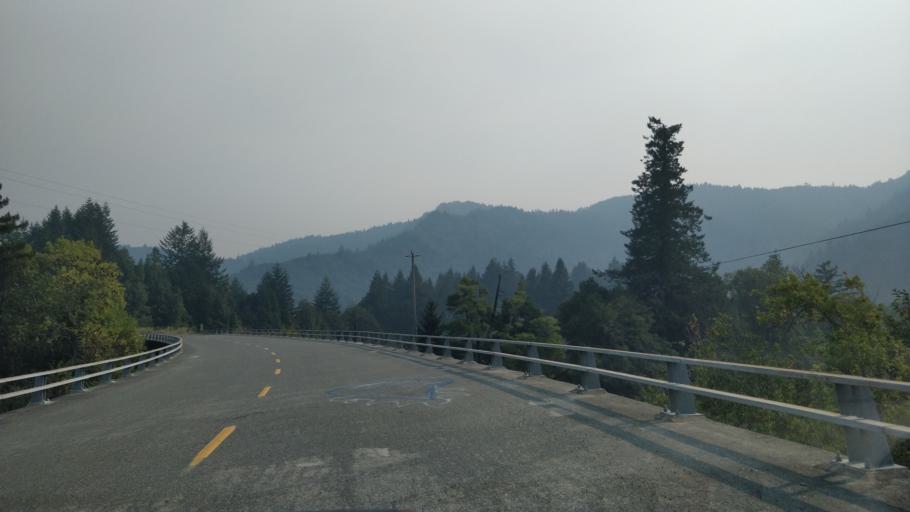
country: US
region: California
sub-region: Humboldt County
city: Rio Dell
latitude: 40.2770
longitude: -124.2430
